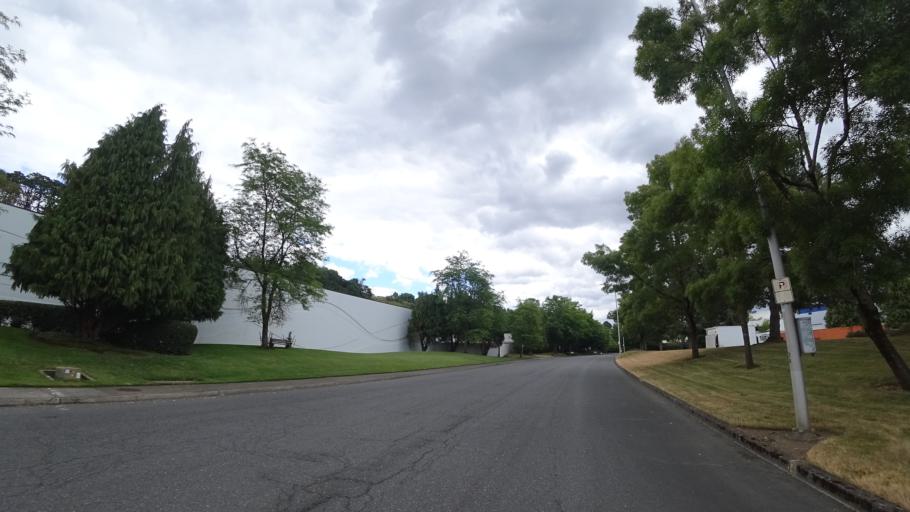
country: US
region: Oregon
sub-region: Multnomah County
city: Portland
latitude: 45.5707
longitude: -122.7031
